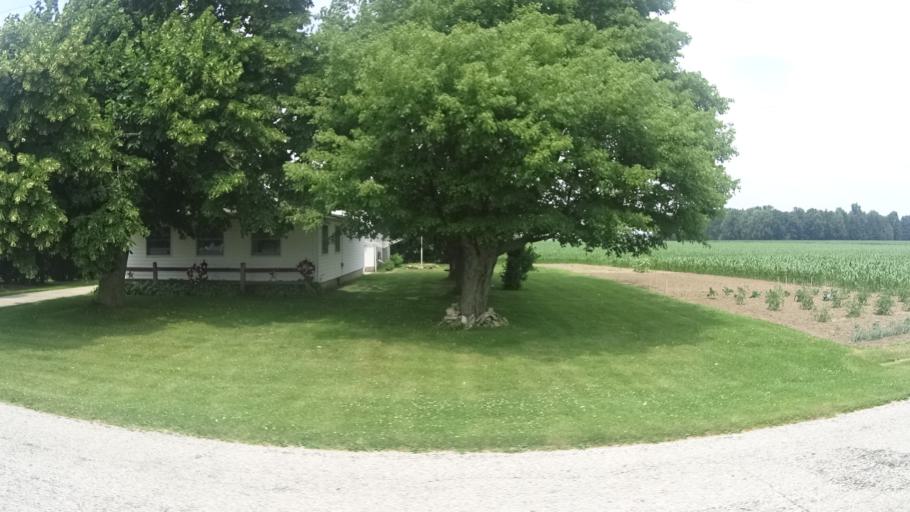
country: US
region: Ohio
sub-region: Erie County
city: Milan
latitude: 41.3076
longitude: -82.6296
